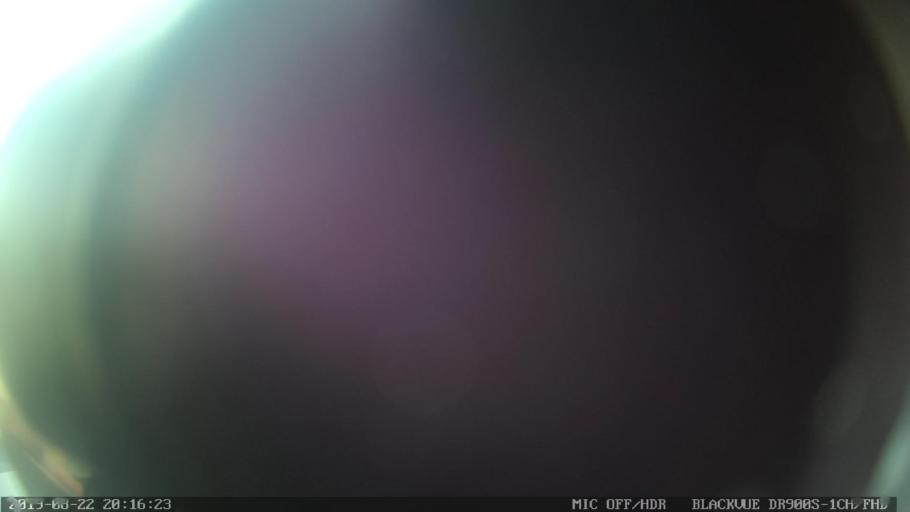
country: PT
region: Guarda
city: Alcains
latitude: 39.9245
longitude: -7.4522
